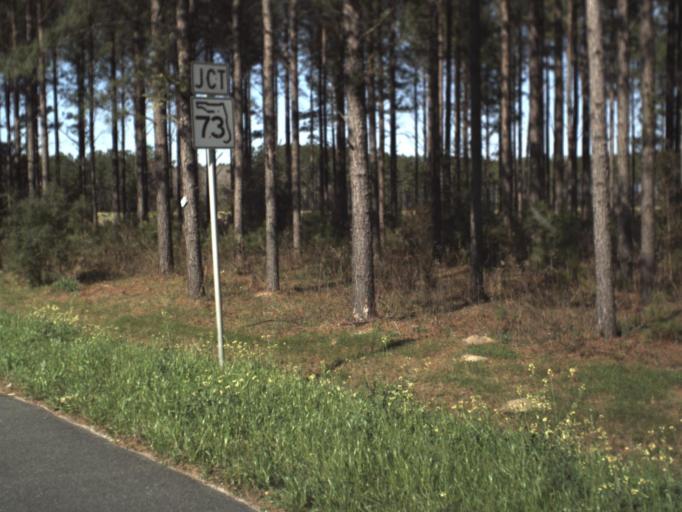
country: US
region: Florida
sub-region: Gulf County
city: Wewahitchka
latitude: 30.2339
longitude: -85.2076
